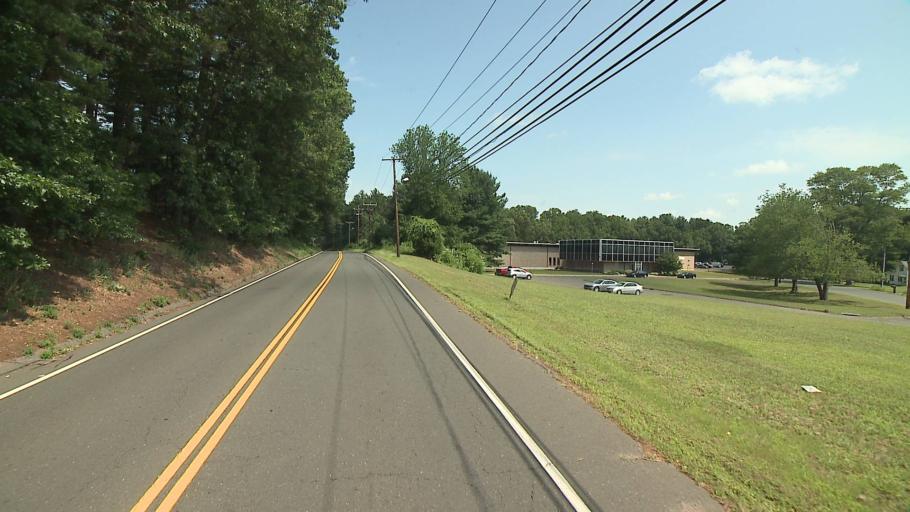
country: US
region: Connecticut
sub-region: Hartford County
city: Plainville
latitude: 41.6868
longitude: -72.8754
